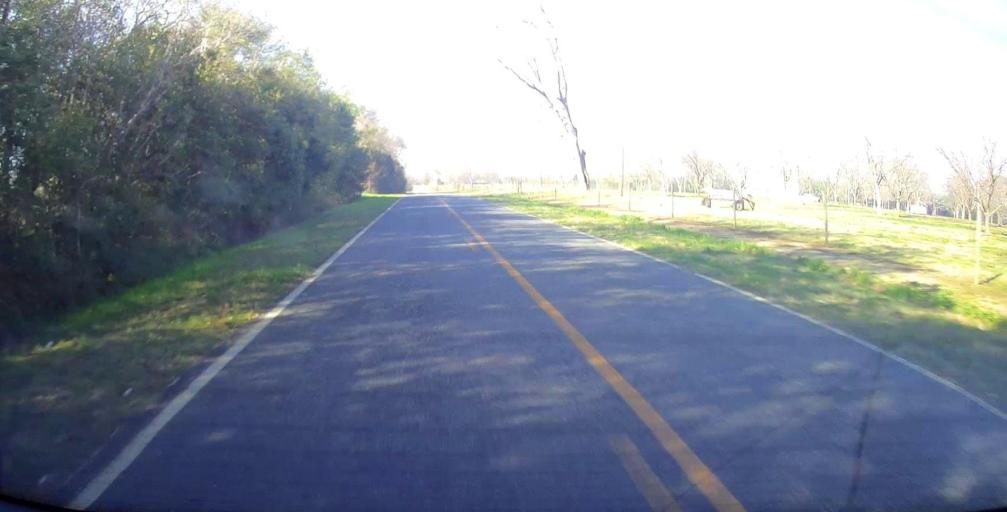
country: US
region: Georgia
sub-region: Peach County
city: Fort Valley
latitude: 32.6097
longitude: -83.8522
